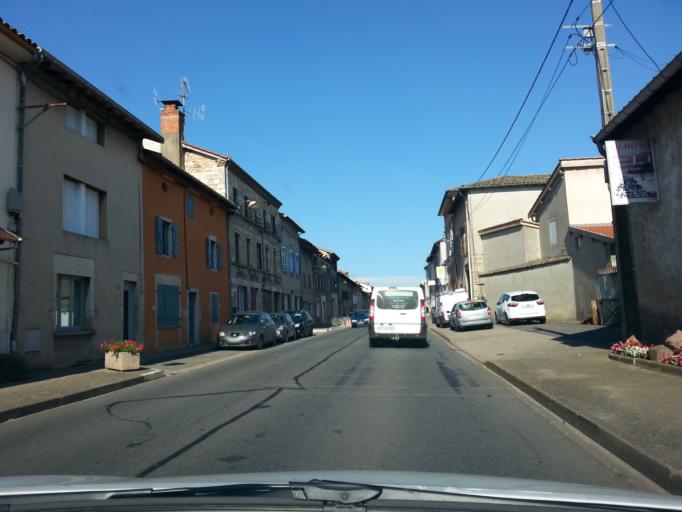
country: FR
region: Rhone-Alpes
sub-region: Departement du Rhone
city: Charentay
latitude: 46.1193
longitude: 4.6679
